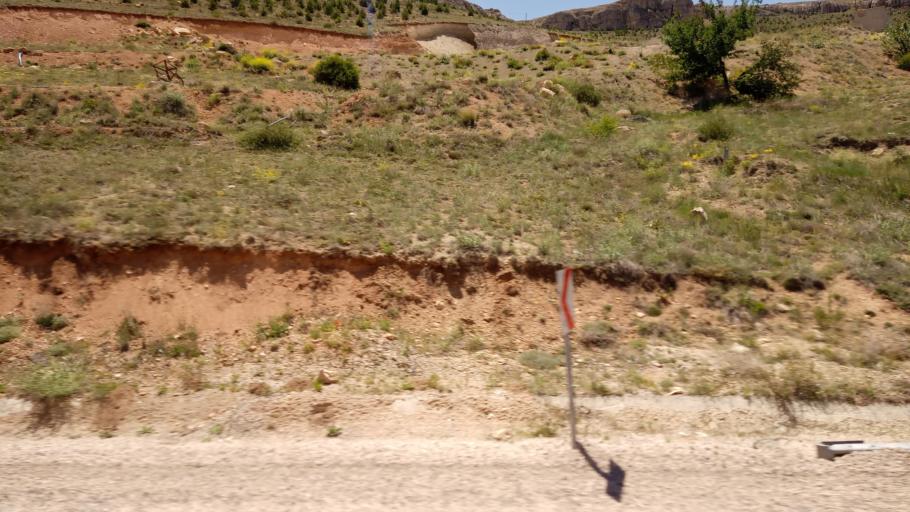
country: TR
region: Malatya
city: Darende
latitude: 38.6147
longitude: 37.4582
